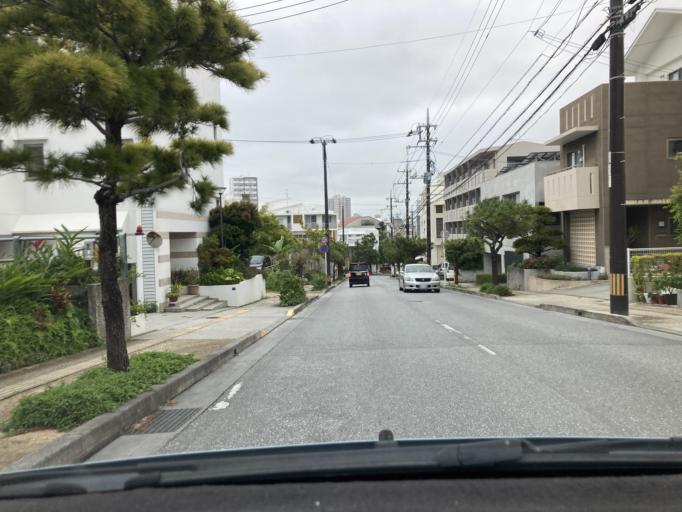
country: JP
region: Okinawa
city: Naha-shi
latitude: 26.2261
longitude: 127.6891
